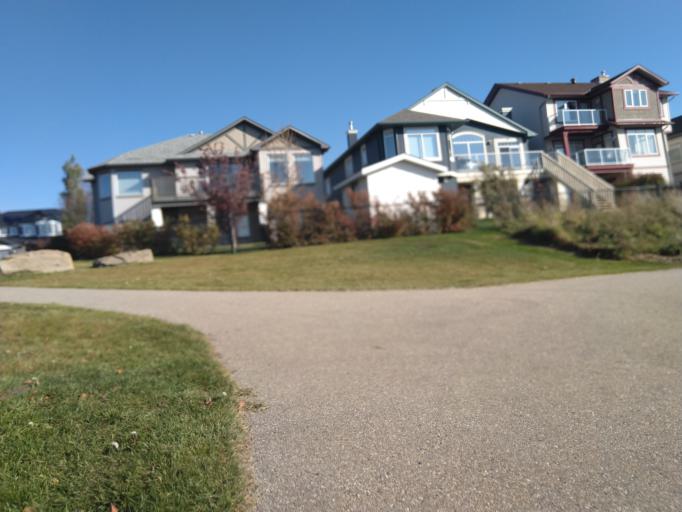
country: CA
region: Alberta
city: Calgary
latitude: 51.1574
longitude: -114.0963
